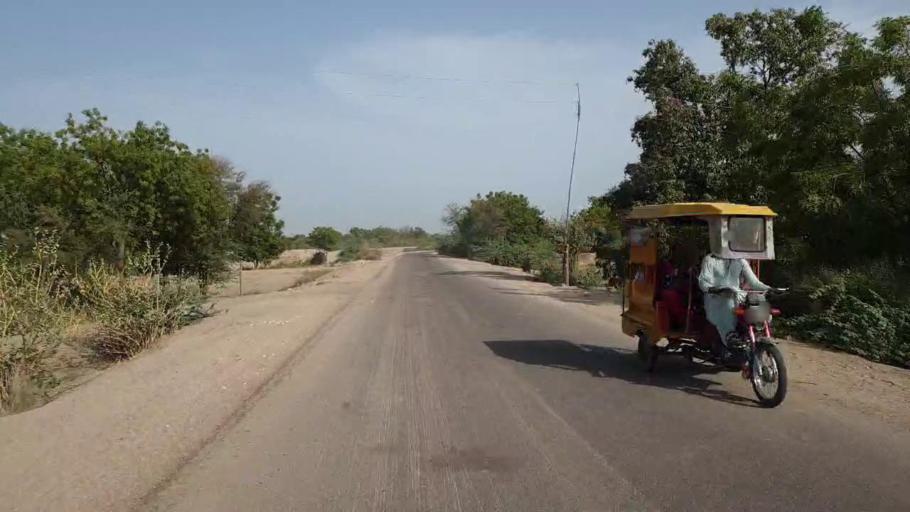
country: PK
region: Sindh
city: Sakrand
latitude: 26.2670
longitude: 68.2801
